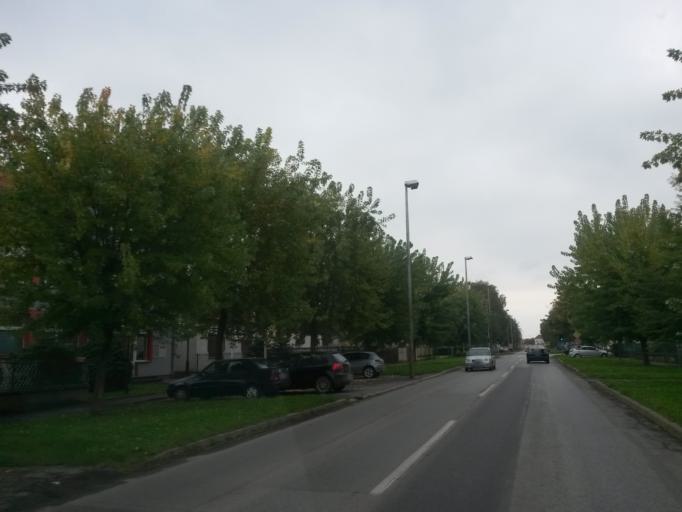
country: HR
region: Osjecko-Baranjska
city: Piskorevci
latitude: 45.3084
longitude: 18.4166
